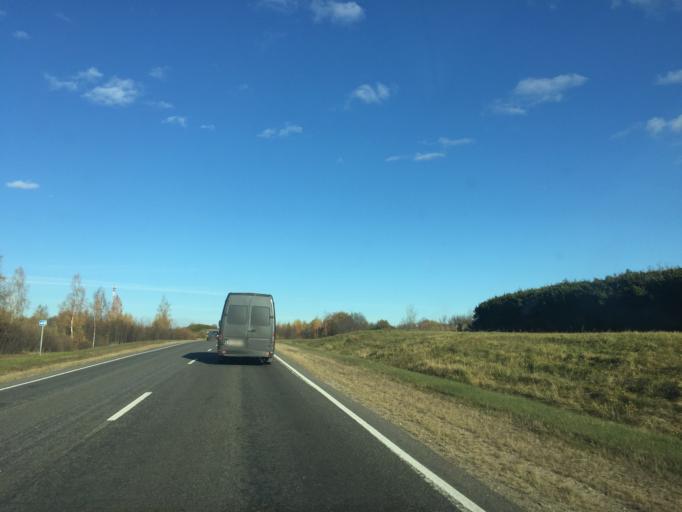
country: BY
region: Vitebsk
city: Dzisna
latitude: 55.2897
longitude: 28.1904
